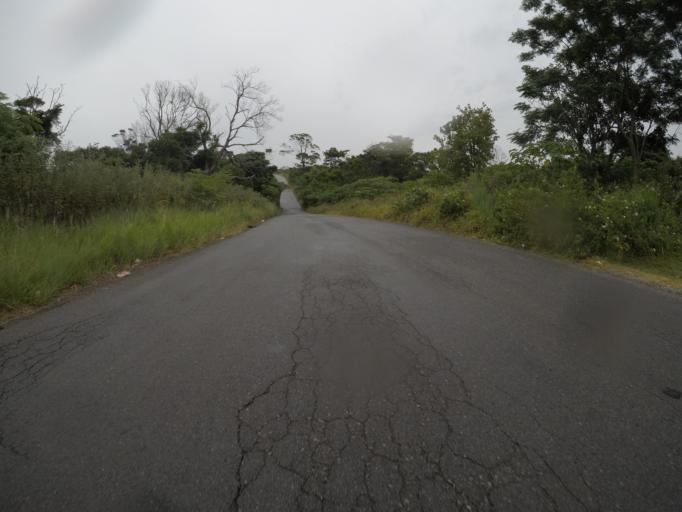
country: ZA
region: Eastern Cape
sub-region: Buffalo City Metropolitan Municipality
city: East London
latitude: -32.9688
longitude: 27.8190
